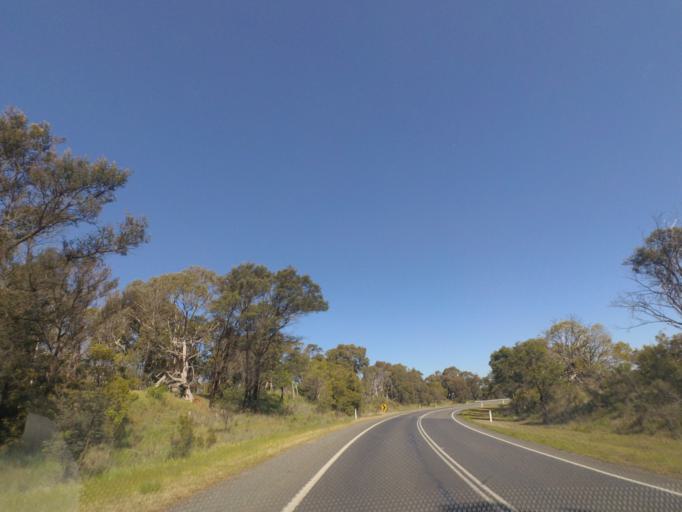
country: AU
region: Victoria
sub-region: Whittlesea
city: Whittlesea
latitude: -37.3287
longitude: 144.9833
